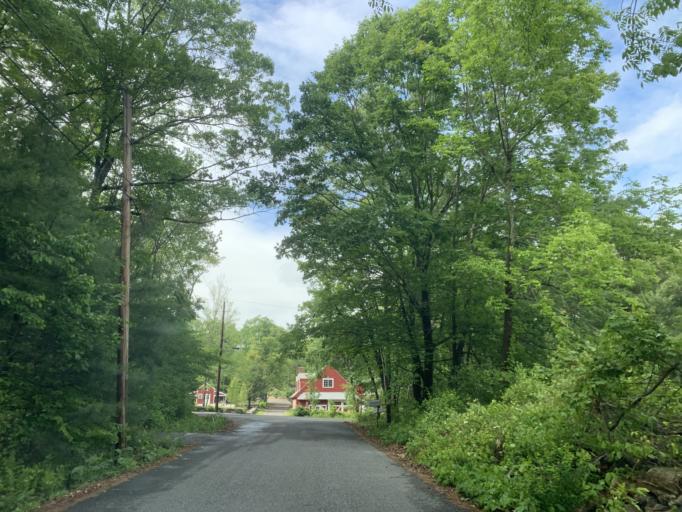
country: US
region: Massachusetts
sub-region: Worcester County
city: Upton
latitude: 42.2013
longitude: -71.6349
